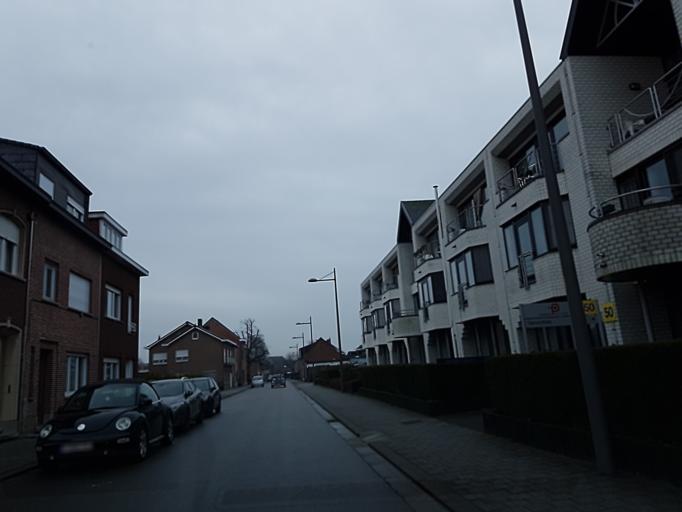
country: BE
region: Flanders
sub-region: Provincie Antwerpen
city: Puurs
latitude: 51.0728
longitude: 4.2800
